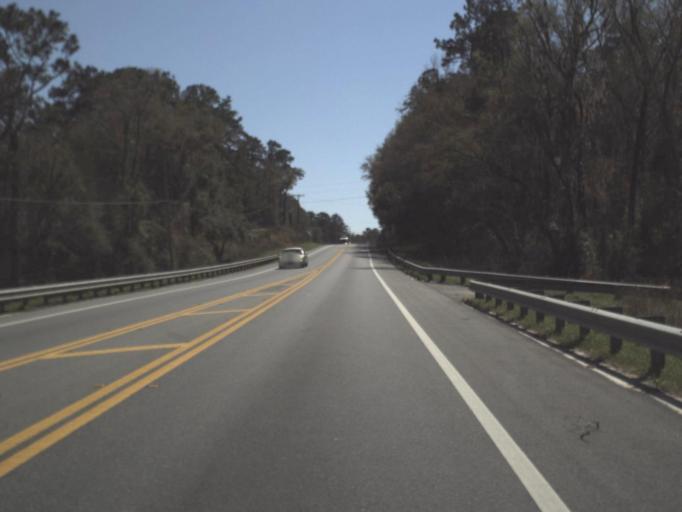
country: US
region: Florida
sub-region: Gadsden County
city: Midway
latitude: 30.4980
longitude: -84.3616
